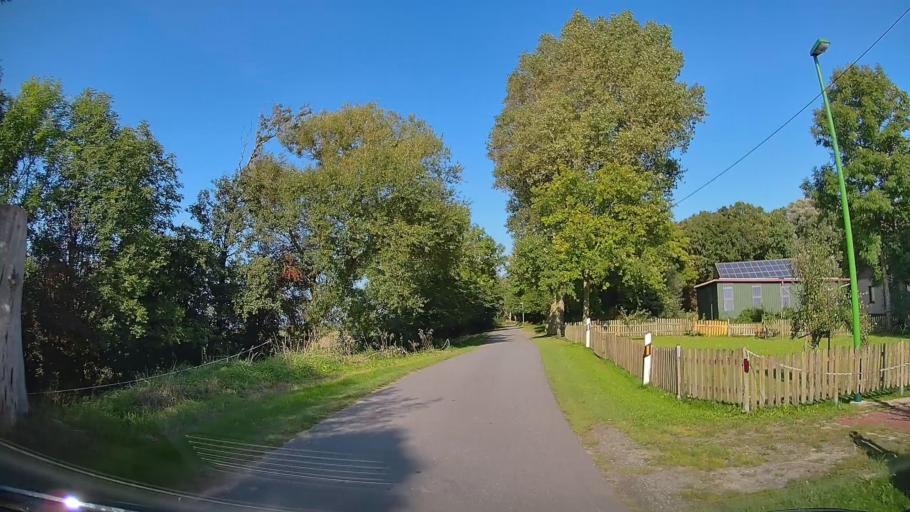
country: DE
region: Lower Saxony
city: Padingbuttel
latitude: 53.7067
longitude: 8.5040
